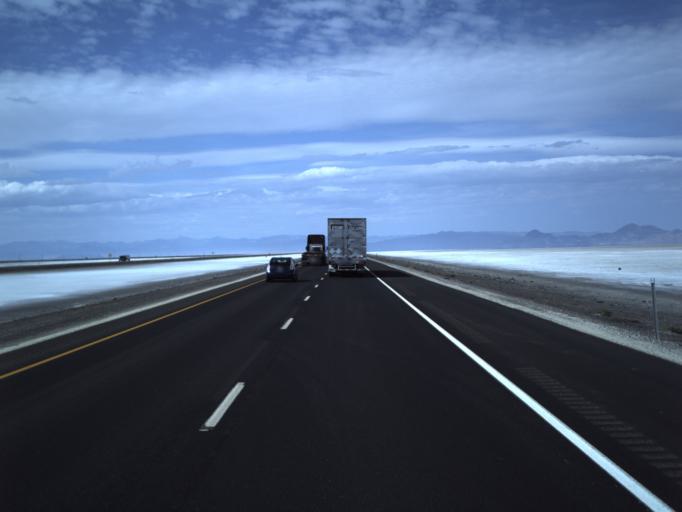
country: US
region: Utah
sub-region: Tooele County
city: Wendover
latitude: 40.7351
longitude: -113.6459
